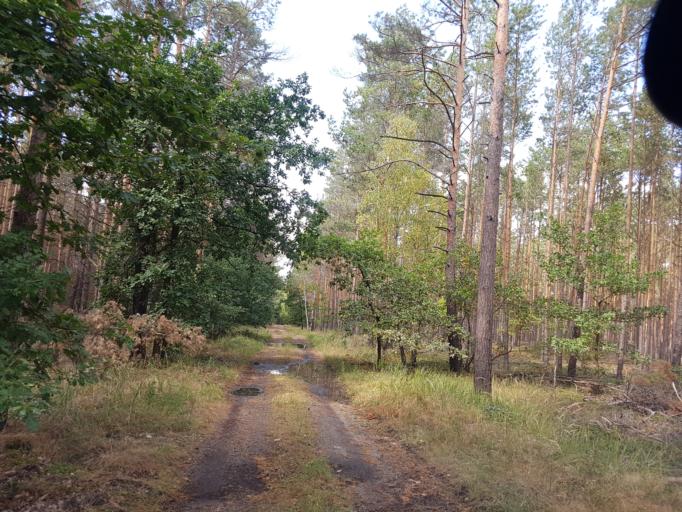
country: DE
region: Brandenburg
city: Finsterwalde
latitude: 51.5935
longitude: 13.7412
